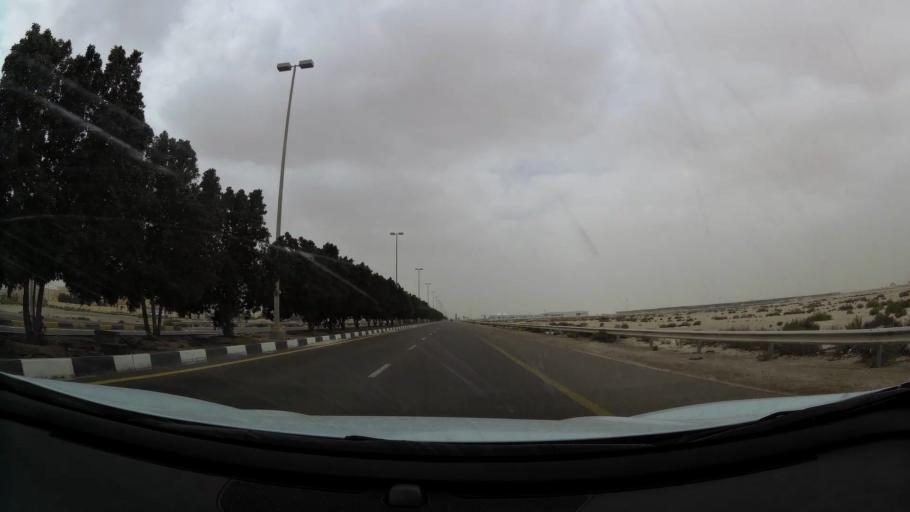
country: AE
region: Abu Dhabi
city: Abu Dhabi
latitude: 24.3987
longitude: 54.6984
